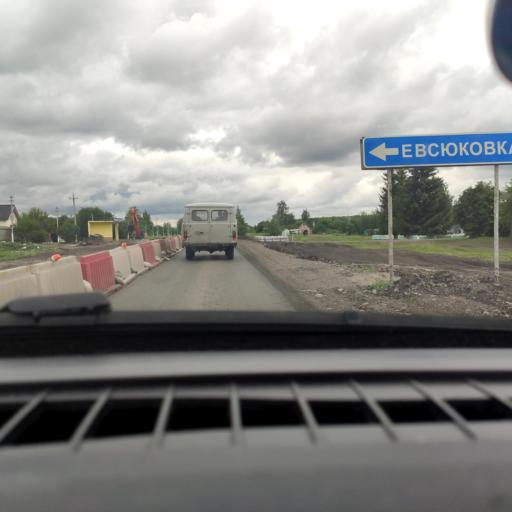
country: RU
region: Lipetsk
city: Usman'
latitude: 51.9523
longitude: 39.7827
